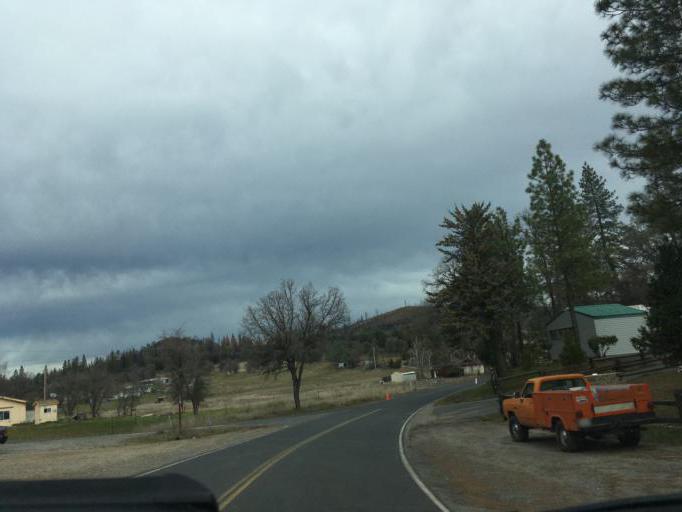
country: US
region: California
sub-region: Calaveras County
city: Mountain Ranch
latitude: 38.2428
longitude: -120.5161
